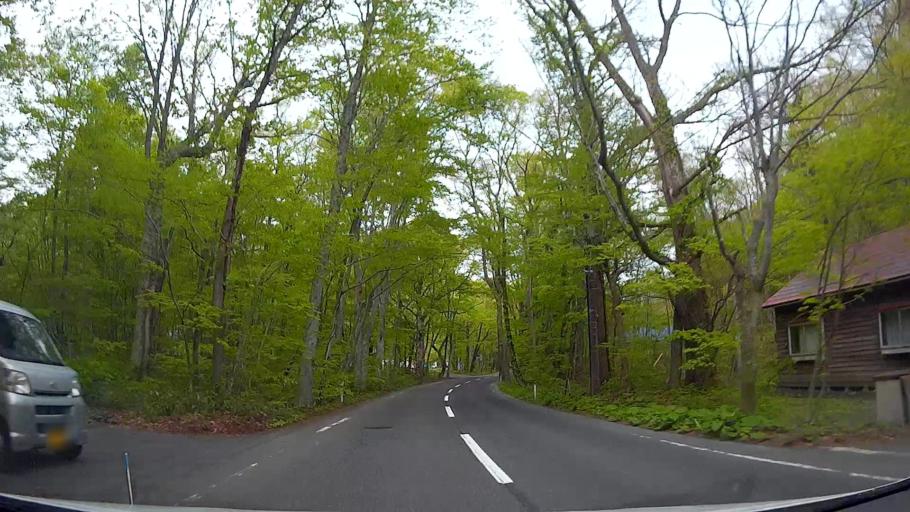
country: JP
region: Aomori
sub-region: Aomori Shi
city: Furudate
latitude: 40.5735
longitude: 140.9783
